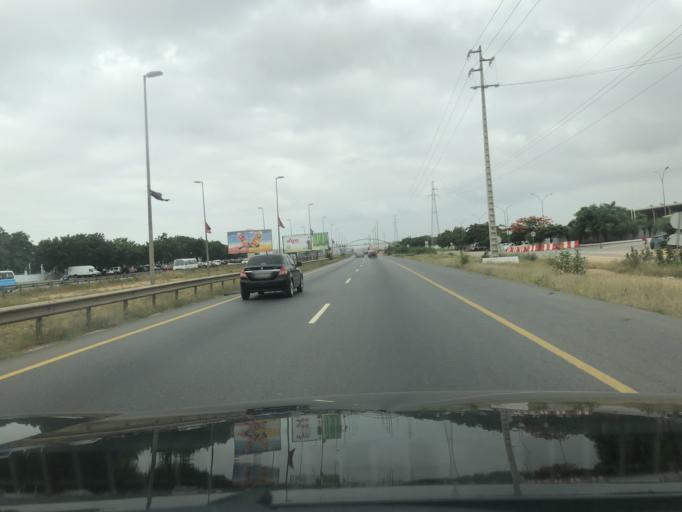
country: AO
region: Luanda
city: Luanda
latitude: -8.9733
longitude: 13.2365
